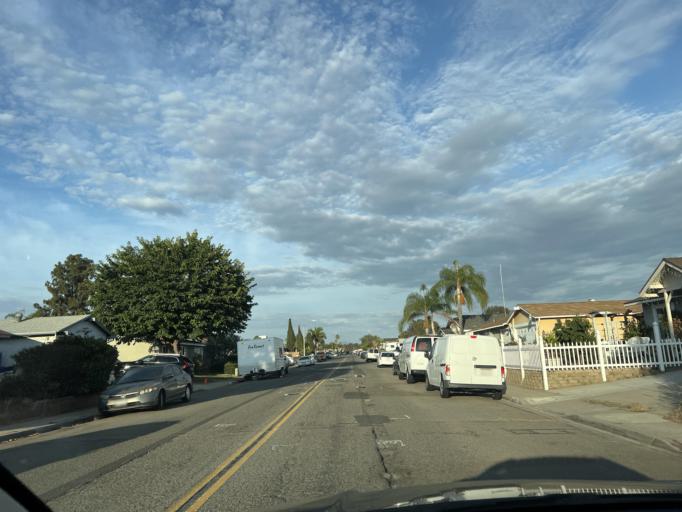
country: US
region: California
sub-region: San Diego County
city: Fairbanks Ranch
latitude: 32.9022
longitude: -117.1390
